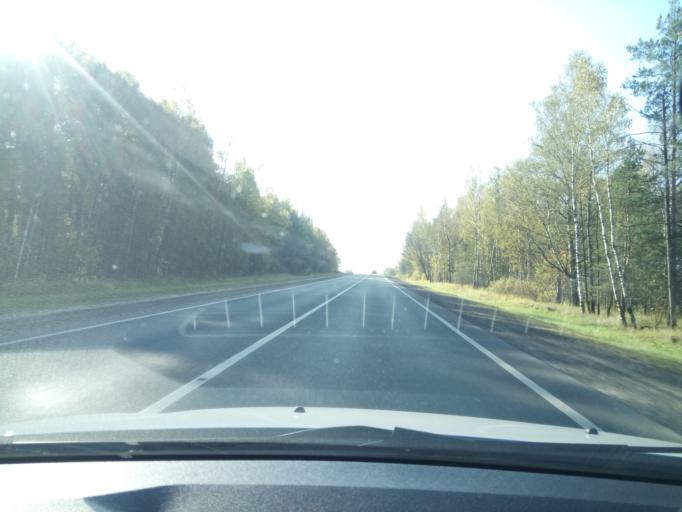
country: RU
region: Nizjnij Novgorod
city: Dal'neye Konstantinovo
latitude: 55.9786
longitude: 43.9720
